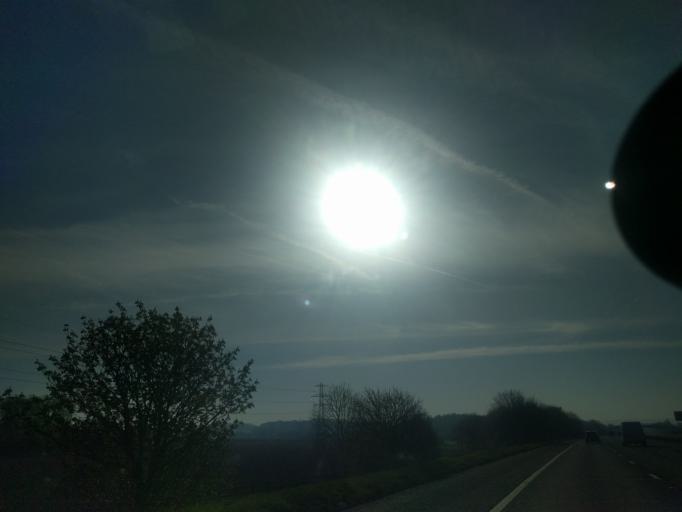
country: GB
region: England
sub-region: Wiltshire
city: Lydiard Tregoze
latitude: 51.5520
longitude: -1.8694
